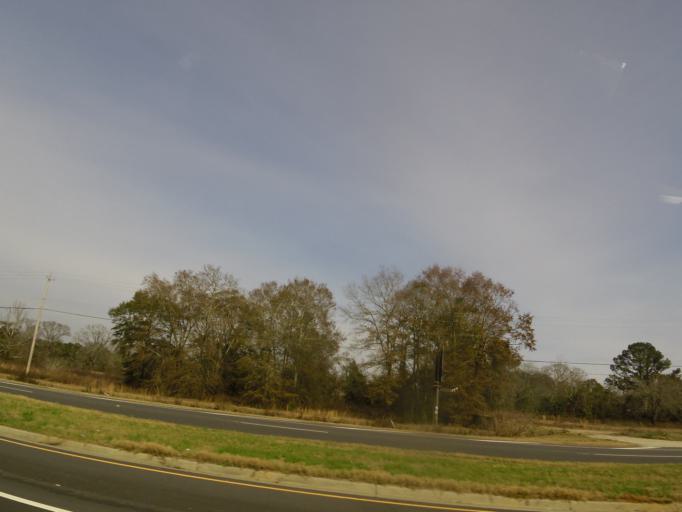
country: US
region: Alabama
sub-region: Dale County
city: Midland City
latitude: 31.2787
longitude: -85.4583
